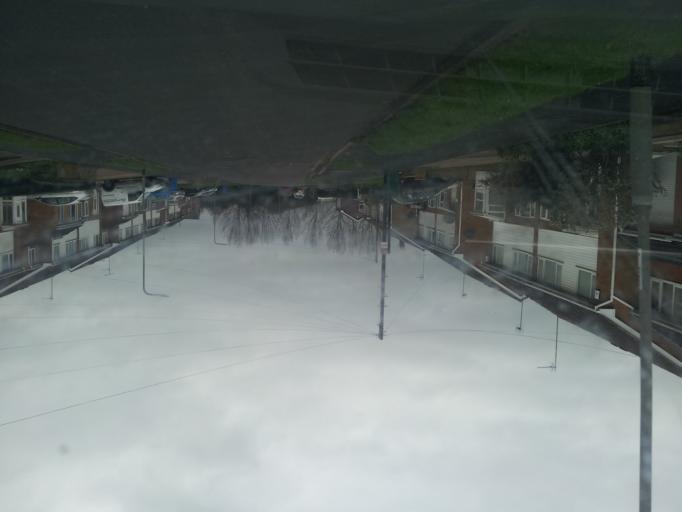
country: GB
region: England
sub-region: Northamptonshire
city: Kettering
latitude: 52.3958
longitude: -0.7015
